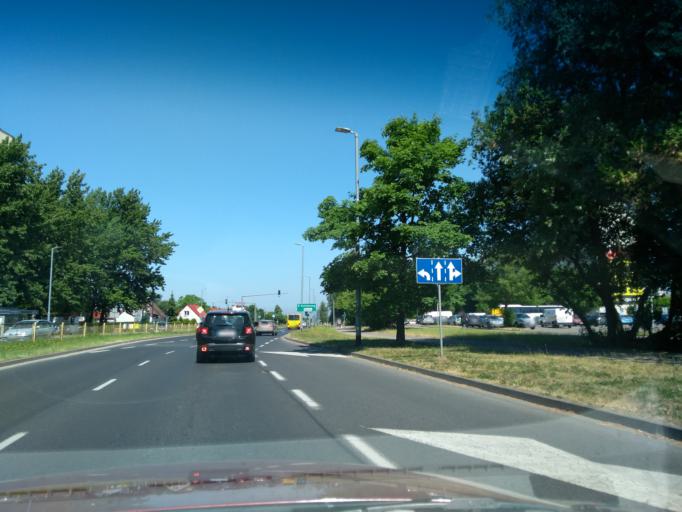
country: PL
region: West Pomeranian Voivodeship
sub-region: Koszalin
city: Koszalin
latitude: 54.2067
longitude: 16.1839
